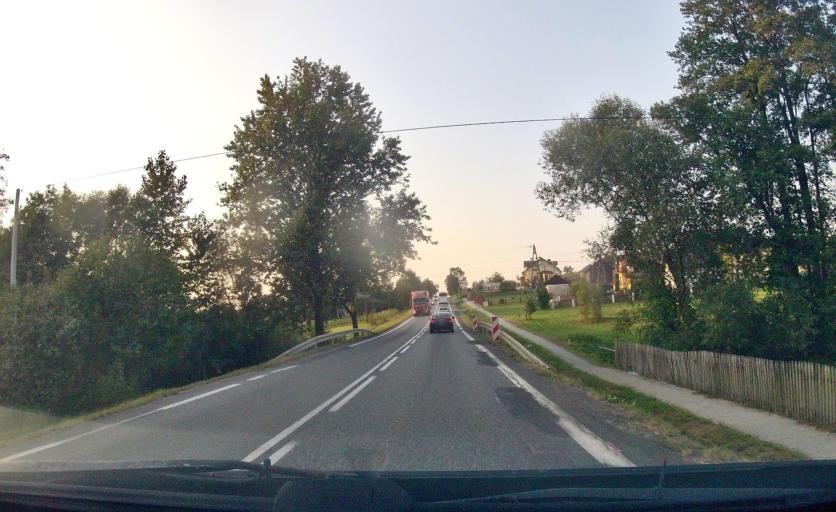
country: PL
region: Subcarpathian Voivodeship
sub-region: Powiat debicki
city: Slotowa
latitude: 49.9160
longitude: 21.3444
